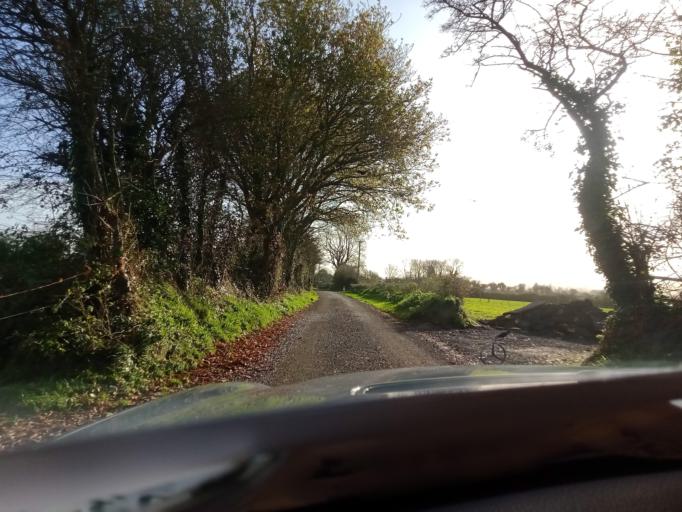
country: IE
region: Leinster
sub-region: Kilkenny
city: Mooncoin
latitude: 52.3165
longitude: -7.2815
